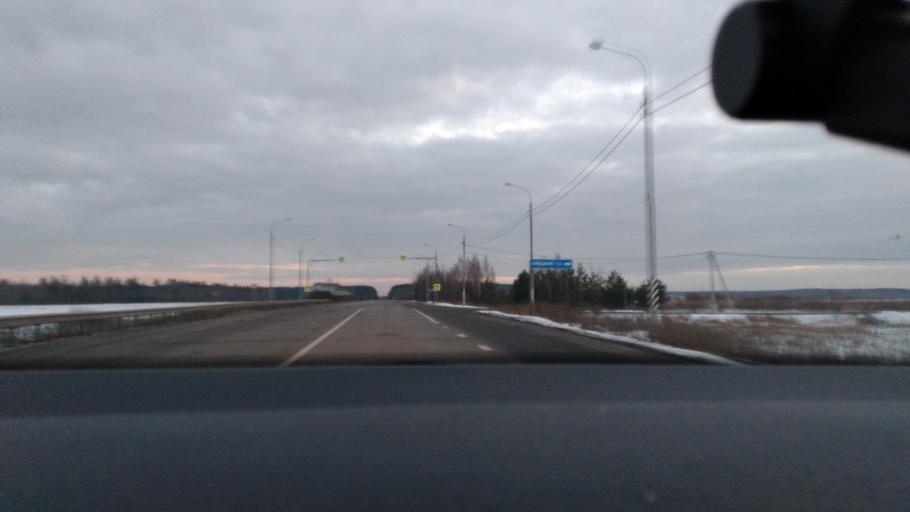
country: RU
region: Moskovskaya
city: Yegor'yevsk
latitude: 55.4398
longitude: 39.0203
